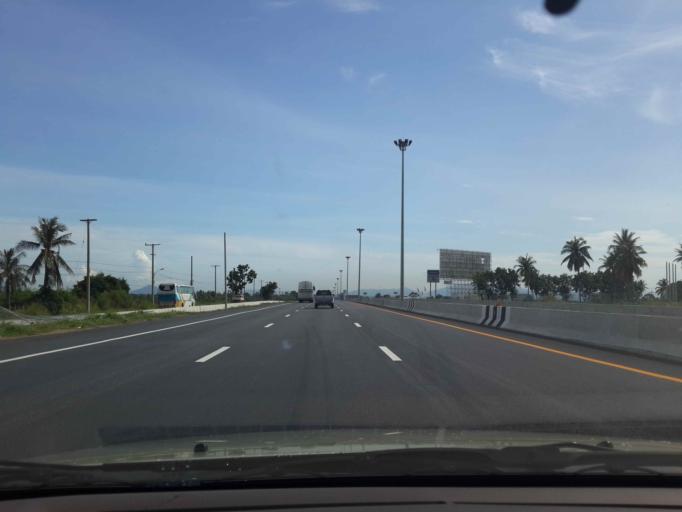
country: TH
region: Chon Buri
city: Ban Talat Bueng
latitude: 13.0318
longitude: 100.9962
